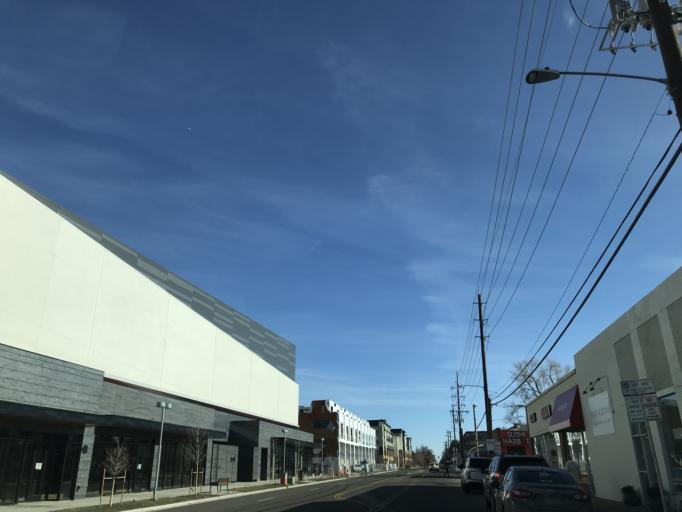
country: US
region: Colorado
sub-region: Arapahoe County
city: Glendale
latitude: 39.7292
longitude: -104.9395
